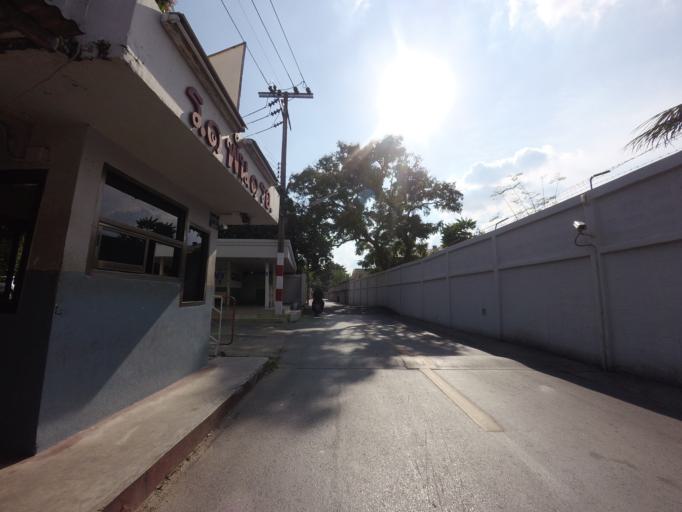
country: TH
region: Bangkok
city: Din Daeng
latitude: 13.7708
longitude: 100.5479
